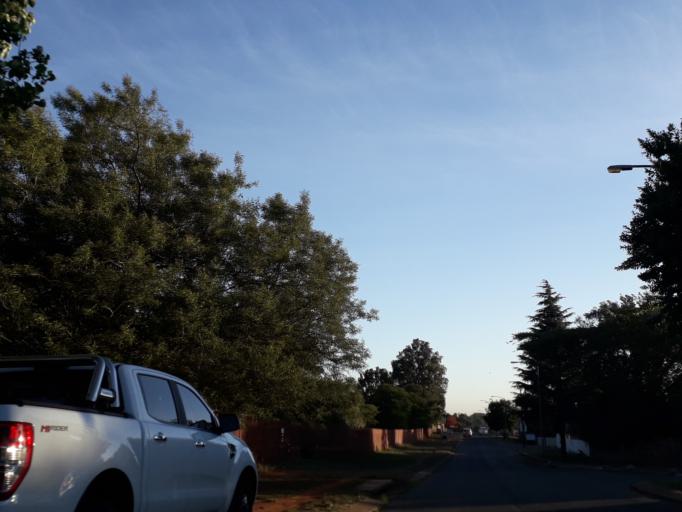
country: ZA
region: Gauteng
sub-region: City of Johannesburg Metropolitan Municipality
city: Roodepoort
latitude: -26.1600
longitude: 27.9524
